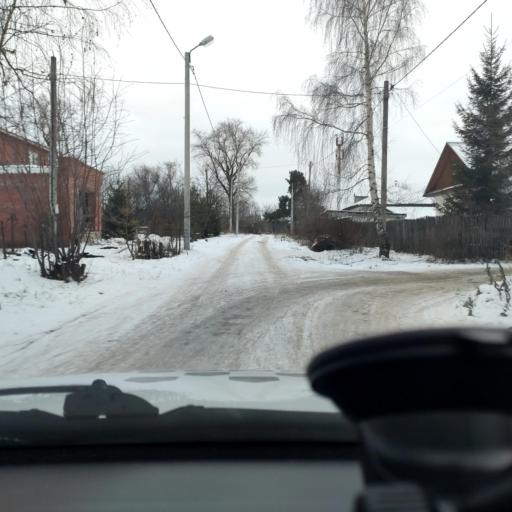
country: RU
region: Perm
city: Froly
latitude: 57.9550
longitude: 56.2870
